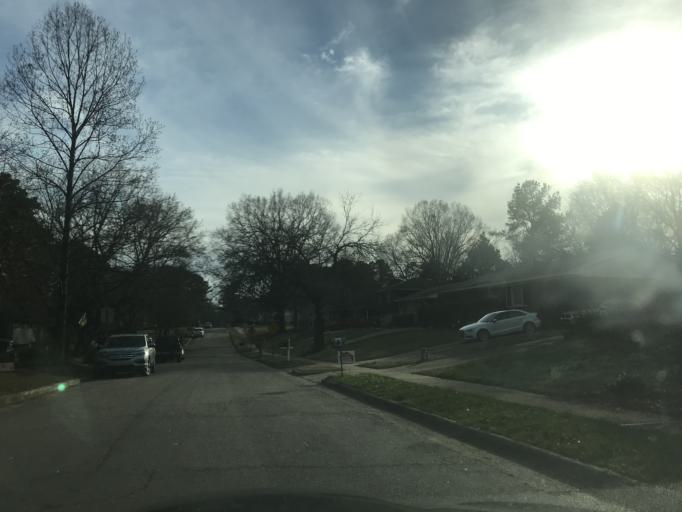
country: US
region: North Carolina
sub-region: Wake County
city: Raleigh
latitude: 35.8323
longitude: -78.5929
